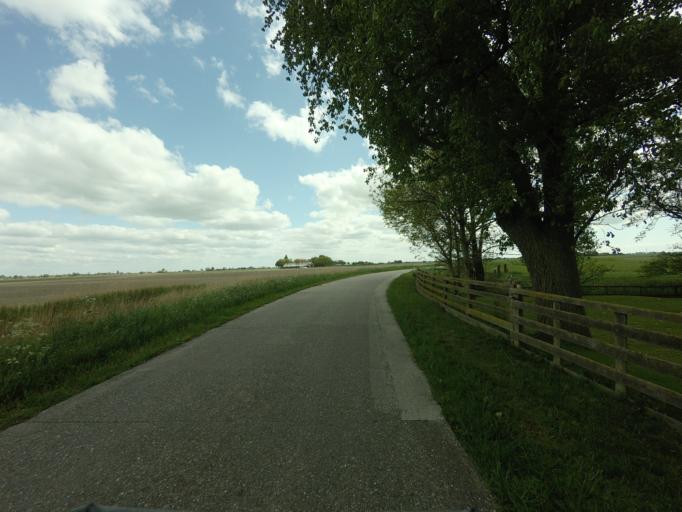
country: NL
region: Friesland
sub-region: Gemeente Littenseradiel
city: Wommels
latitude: 53.1166
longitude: 5.5507
